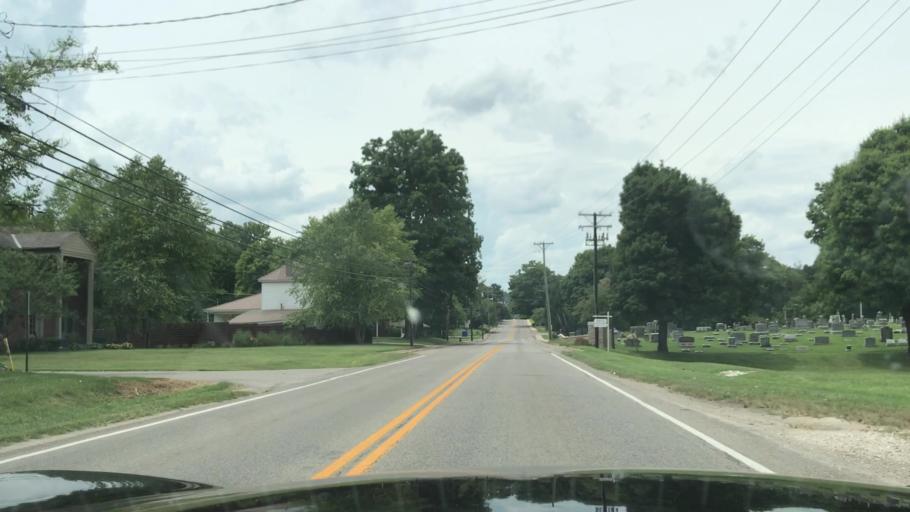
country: US
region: Kentucky
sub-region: Hart County
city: Horse Cave
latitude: 37.1786
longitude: -85.8972
